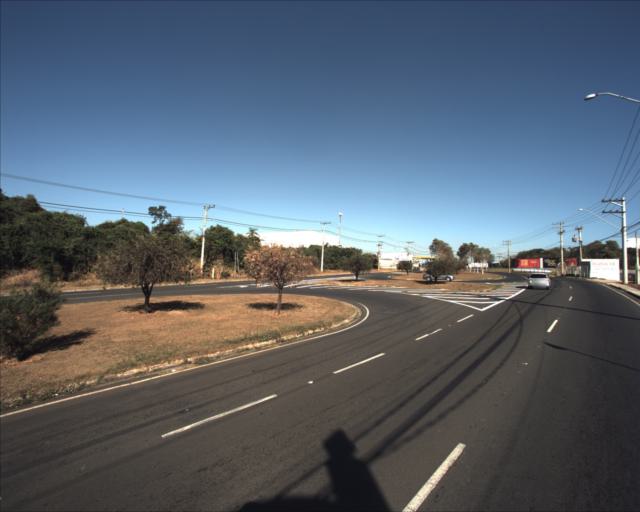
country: BR
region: Sao Paulo
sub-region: Sorocaba
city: Sorocaba
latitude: -23.4539
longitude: -47.4186
